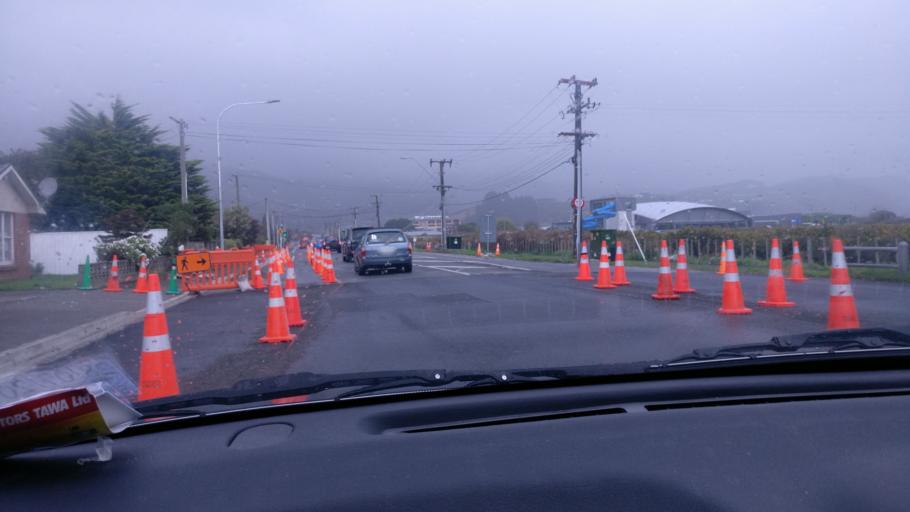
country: NZ
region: Wellington
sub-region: Kapiti Coast District
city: Paraparaumu
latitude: -40.9102
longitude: 175.0016
